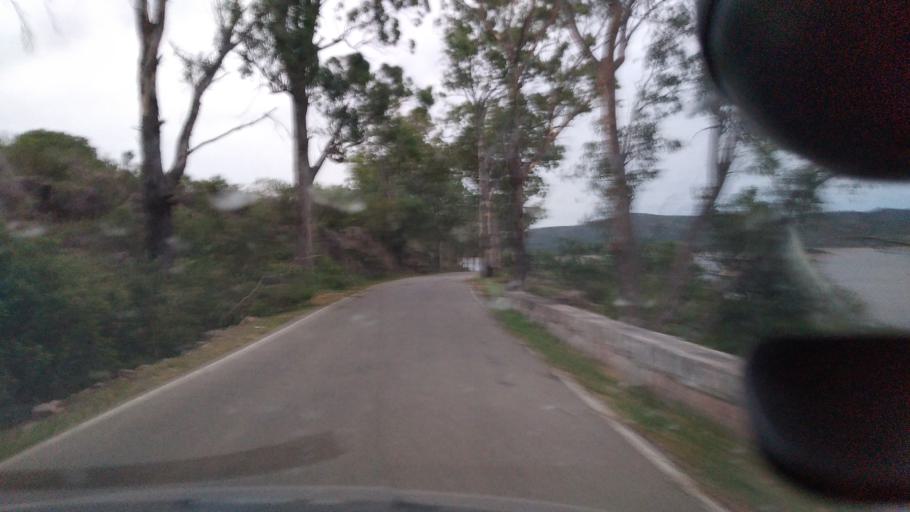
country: AR
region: Cordoba
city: Villa Las Rosas
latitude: -31.8768
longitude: -65.0290
